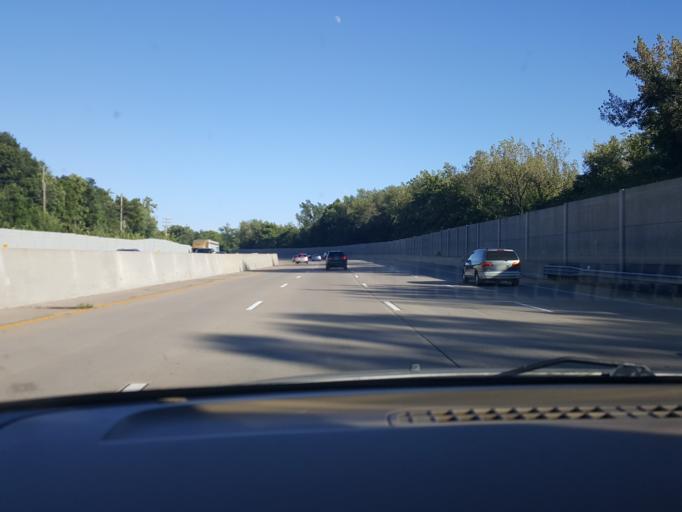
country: US
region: Missouri
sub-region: Saint Louis County
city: Ladue
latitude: 38.6338
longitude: -90.3890
